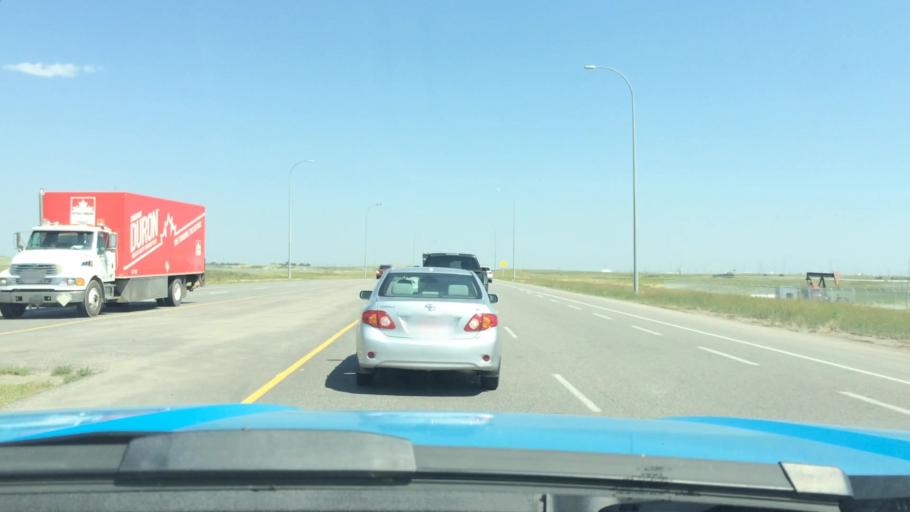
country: CA
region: Alberta
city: Chestermere
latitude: 51.0148
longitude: -113.9521
